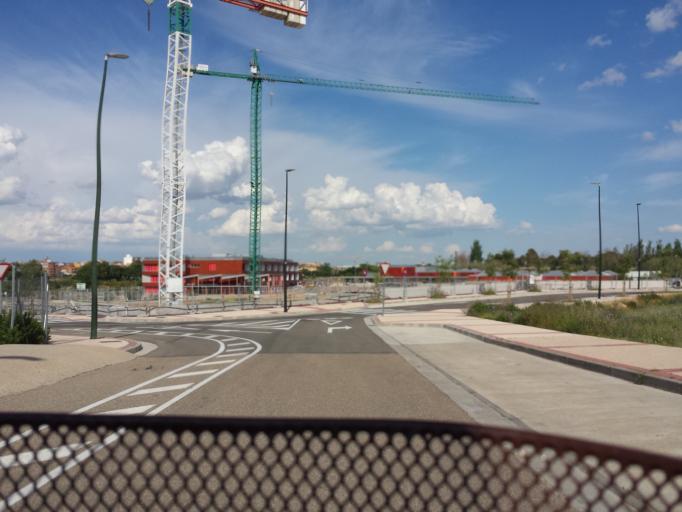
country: ES
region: Aragon
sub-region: Provincia de Zaragoza
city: Montecanal
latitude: 41.6354
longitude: -0.9434
